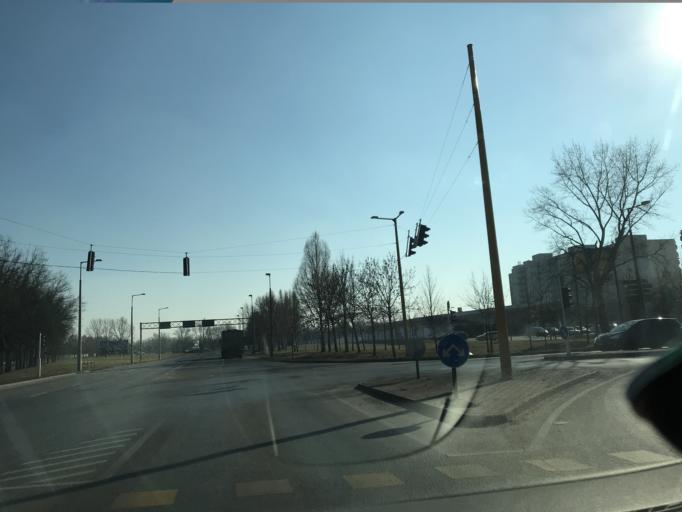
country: HU
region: Gyor-Moson-Sopron
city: Gyor
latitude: 47.6643
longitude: 17.6367
